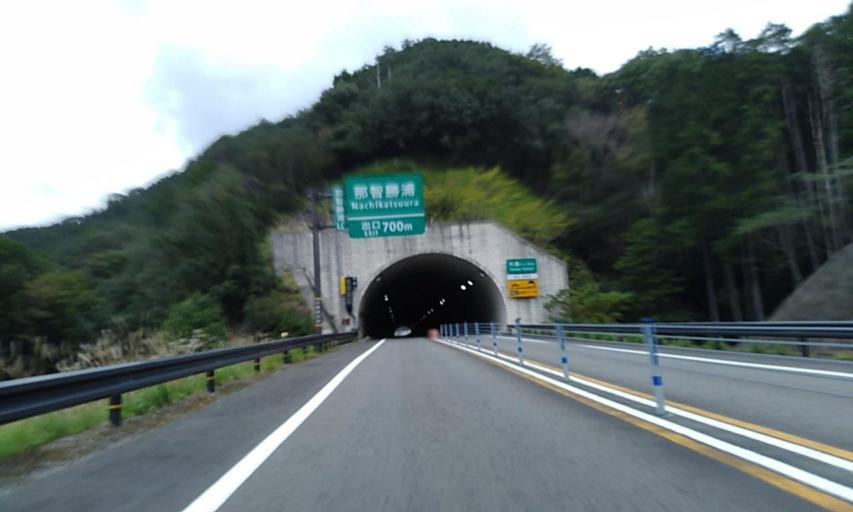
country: JP
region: Wakayama
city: Shingu
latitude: 33.6352
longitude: 135.9251
